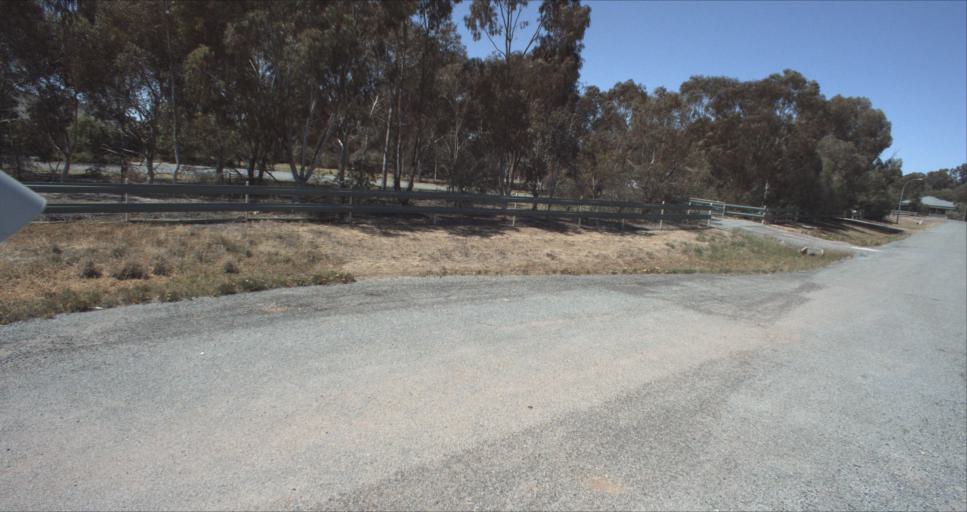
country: AU
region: New South Wales
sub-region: Leeton
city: Leeton
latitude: -34.5293
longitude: 146.3950
